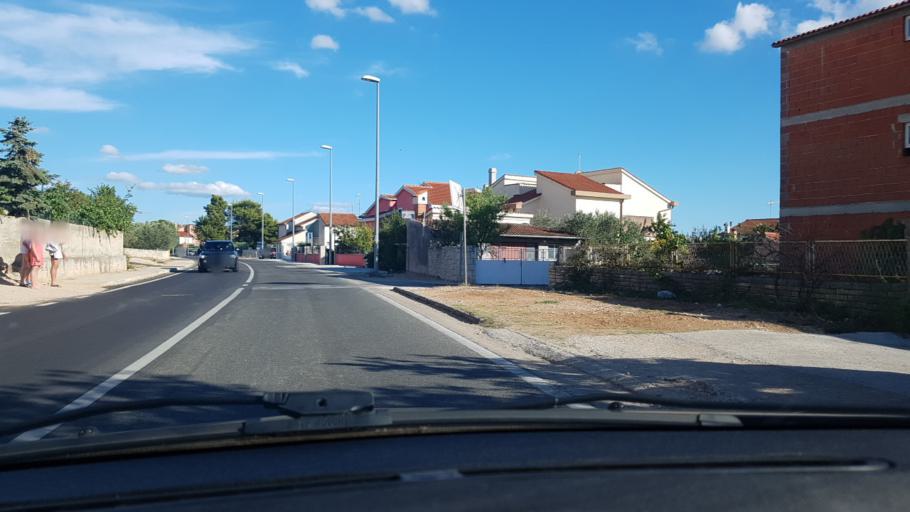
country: HR
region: Sibensko-Kniniska
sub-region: Grad Sibenik
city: Brodarica
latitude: 43.6842
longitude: 15.9122
